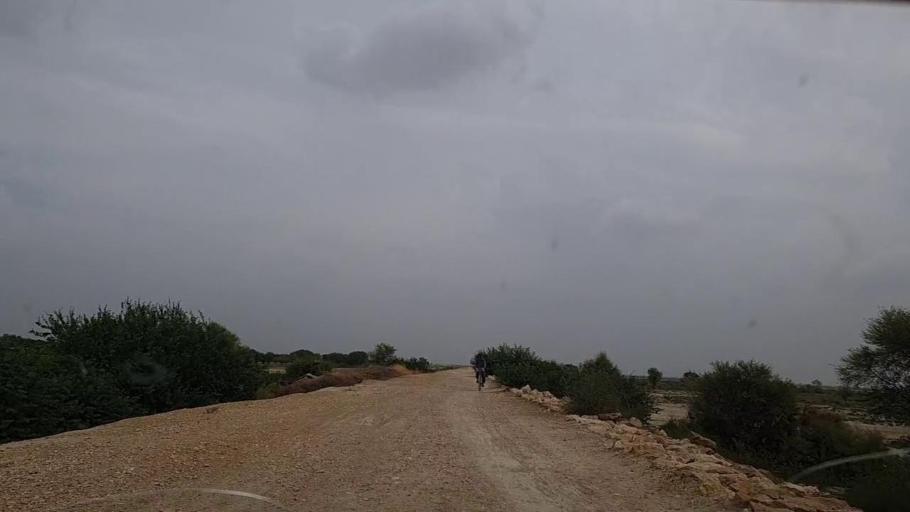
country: PK
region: Sindh
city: Johi
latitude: 26.7191
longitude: 67.5801
